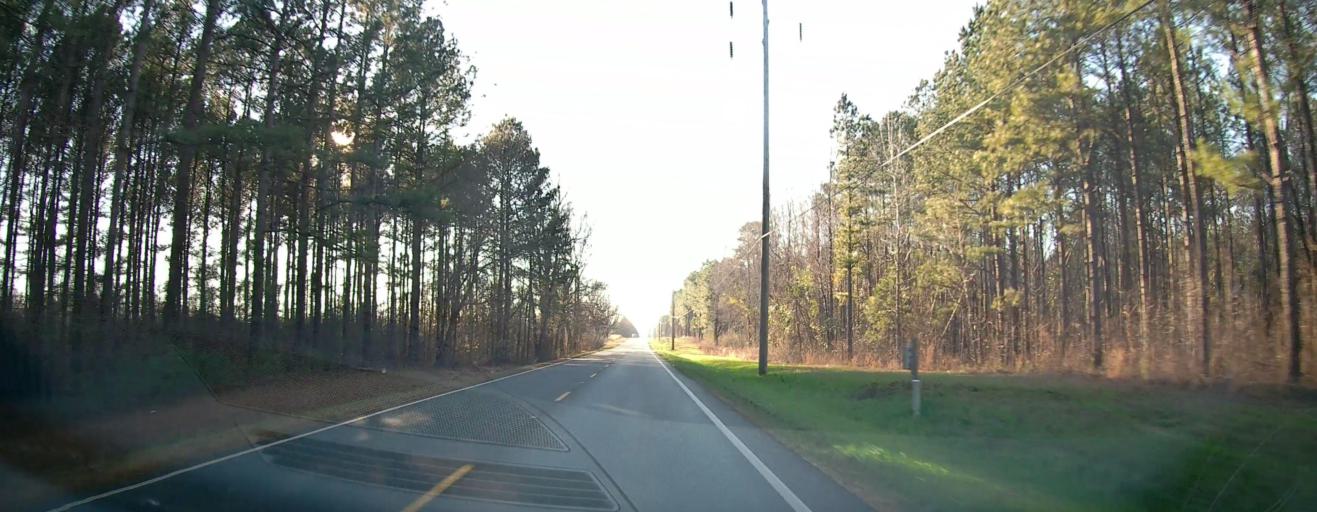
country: US
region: Georgia
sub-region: Harris County
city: Pine Mountain
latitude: 32.9162
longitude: -84.7832
